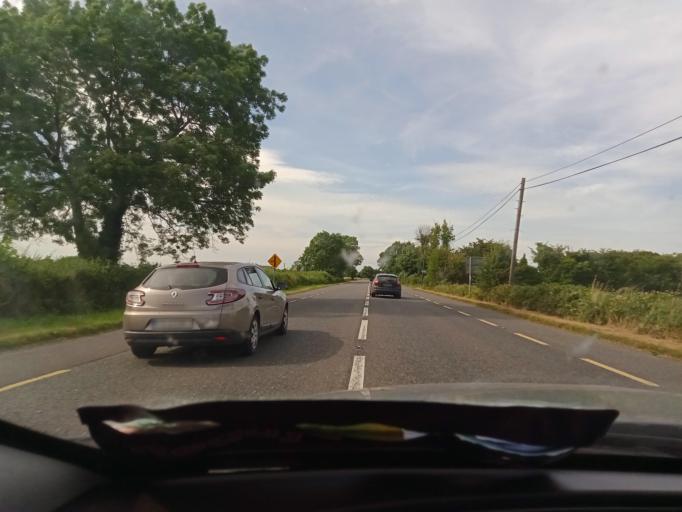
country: IE
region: Leinster
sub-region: Uibh Fhaili
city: Tullamore
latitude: 53.2334
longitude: -7.4767
